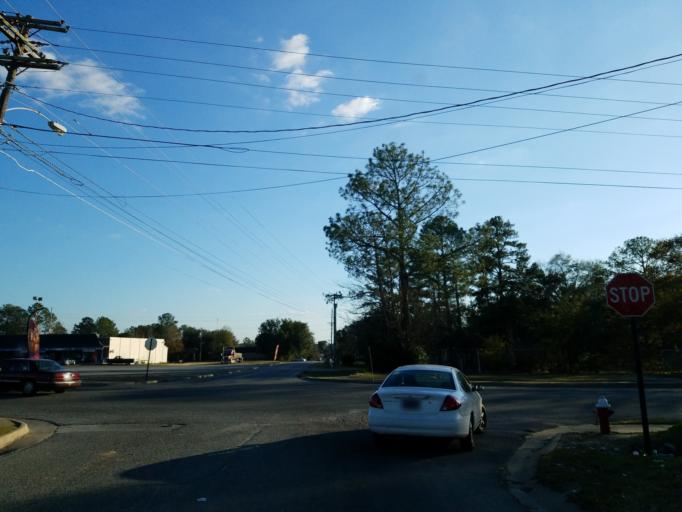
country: US
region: Georgia
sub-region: Crisp County
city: Cordele
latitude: 31.9553
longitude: -83.7862
